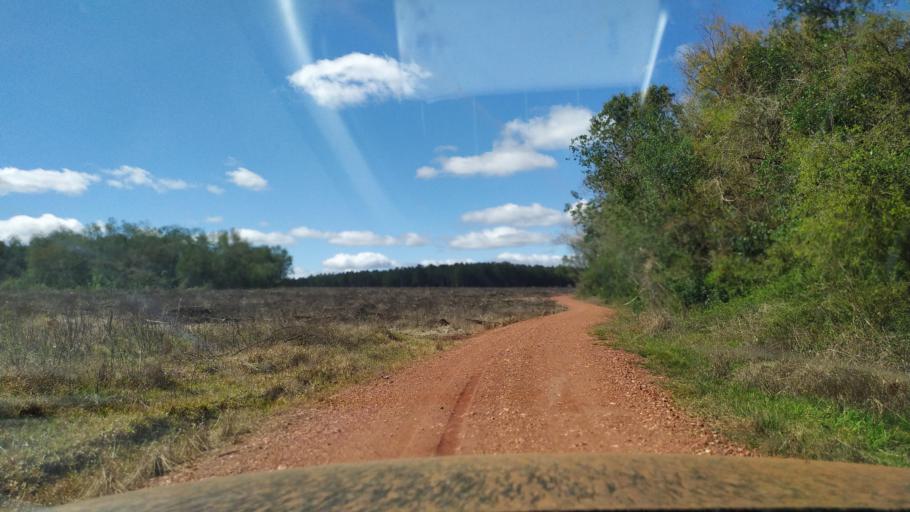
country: AR
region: Corrientes
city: Gobernador Ingeniero Valentin Virasoro
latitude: -28.2902
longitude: -56.0497
